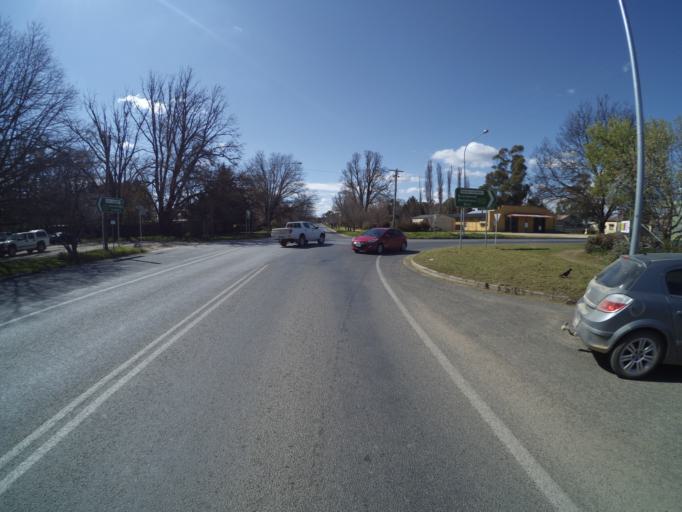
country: AU
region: New South Wales
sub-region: Palerang
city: Bungendore
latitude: -35.2562
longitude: 149.4379
